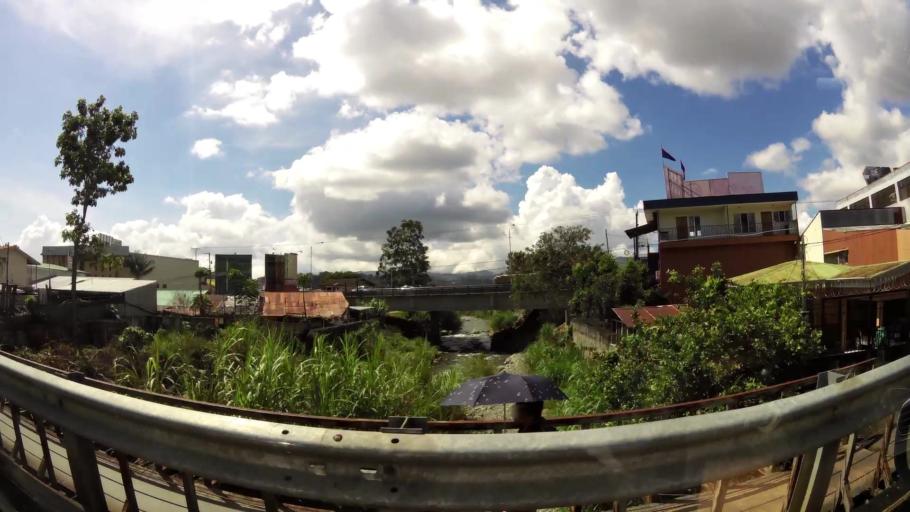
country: CR
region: San Jose
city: San Isidro
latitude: 9.3728
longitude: -83.7004
